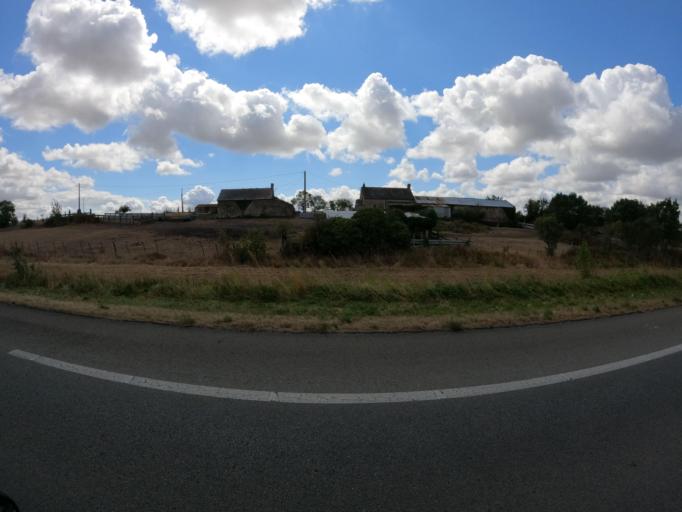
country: FR
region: Pays de la Loire
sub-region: Departement de la Loire-Atlantique
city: Ancenis
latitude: 47.4100
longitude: -1.1559
